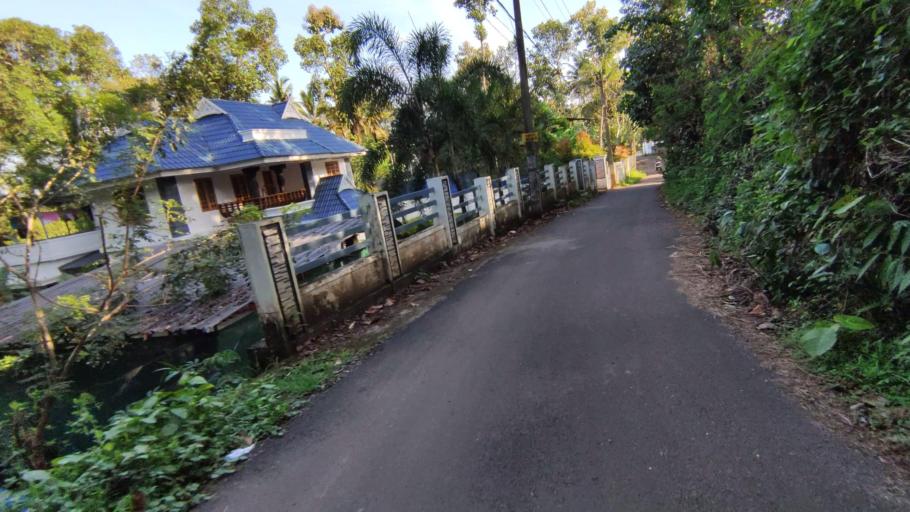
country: IN
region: Kerala
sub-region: Kottayam
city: Kottayam
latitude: 9.5971
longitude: 76.4831
